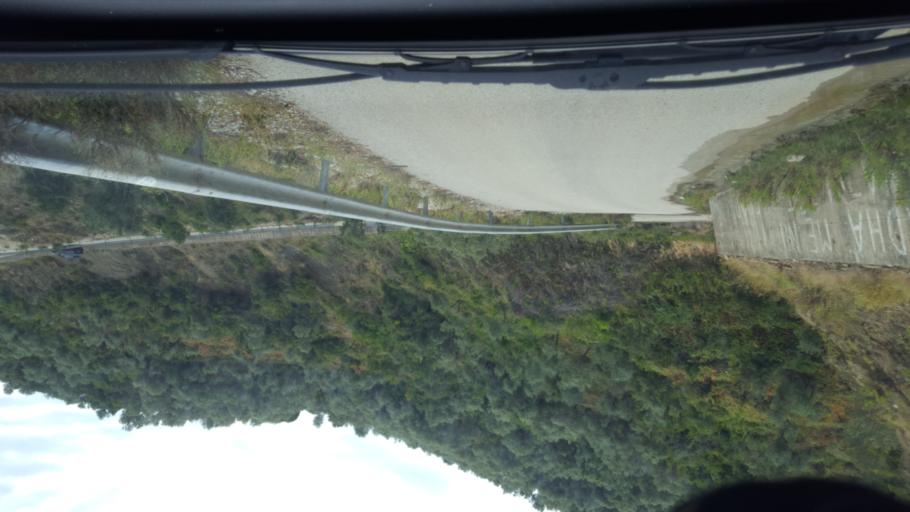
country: AL
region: Vlore
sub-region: Rrethi i Sarandes
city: Lukove
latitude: 39.9850
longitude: 19.9168
